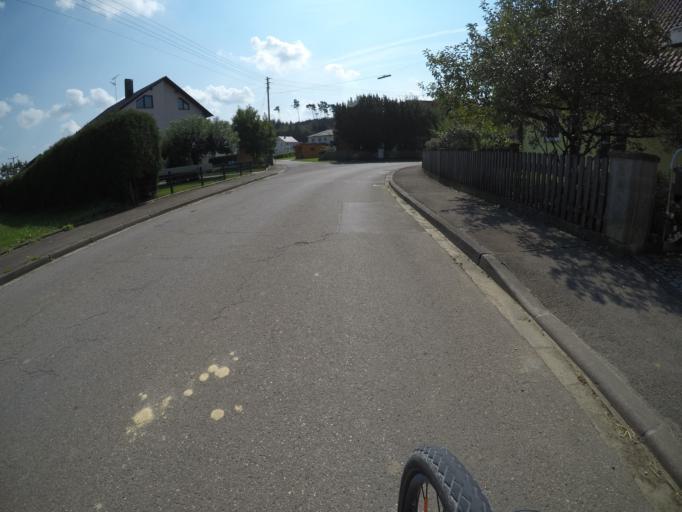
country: DE
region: Bavaria
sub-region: Swabia
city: Laugna
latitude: 48.5522
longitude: 10.7167
